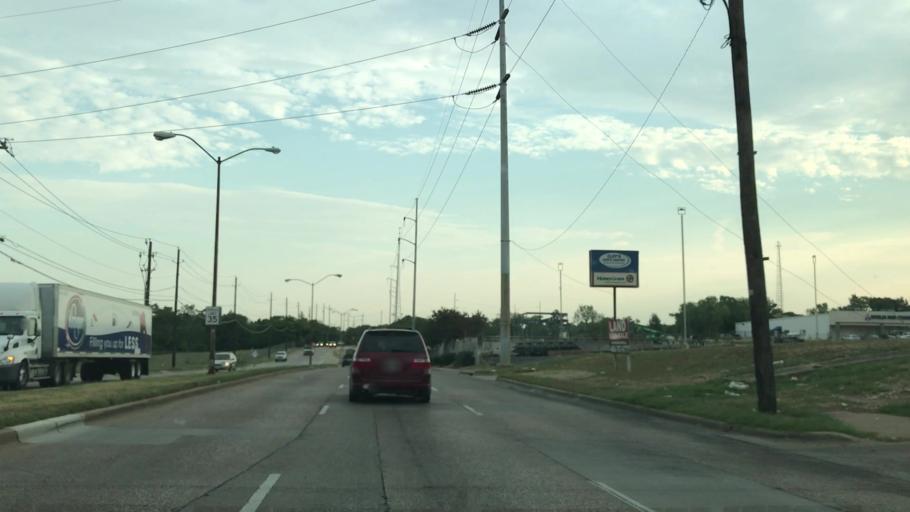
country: US
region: Texas
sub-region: Dallas County
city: Cockrell Hill
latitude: 32.7548
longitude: -96.8740
